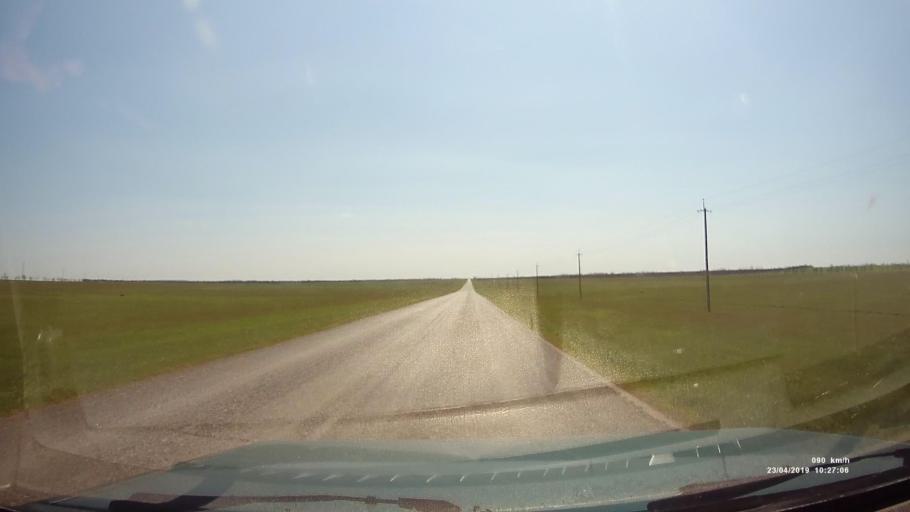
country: RU
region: Kalmykiya
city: Yashalta
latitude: 46.6165
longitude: 42.4857
